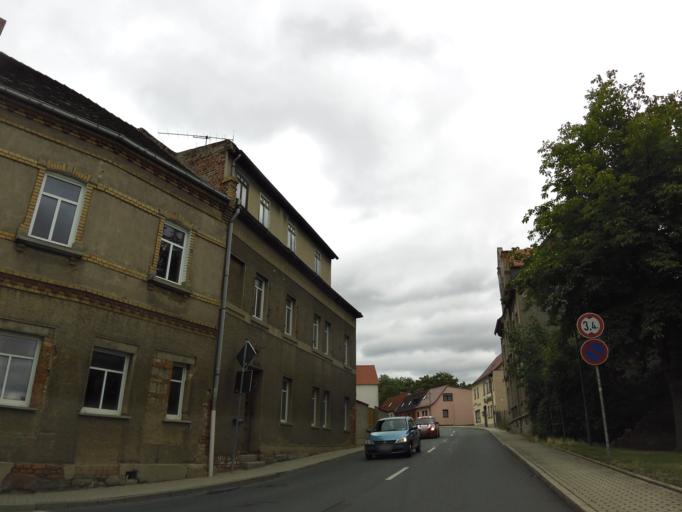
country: DE
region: Saxony-Anhalt
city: Teuchern
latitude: 51.1224
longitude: 12.0254
